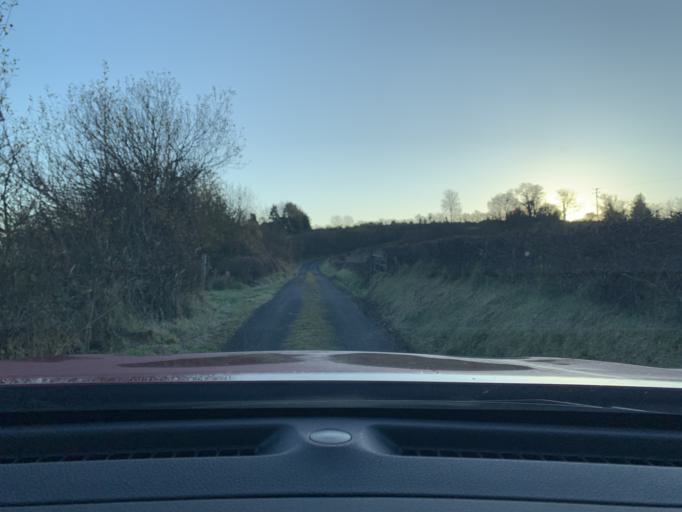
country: IE
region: Connaught
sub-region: Sligo
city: Ballymote
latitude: 54.0670
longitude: -8.5371
